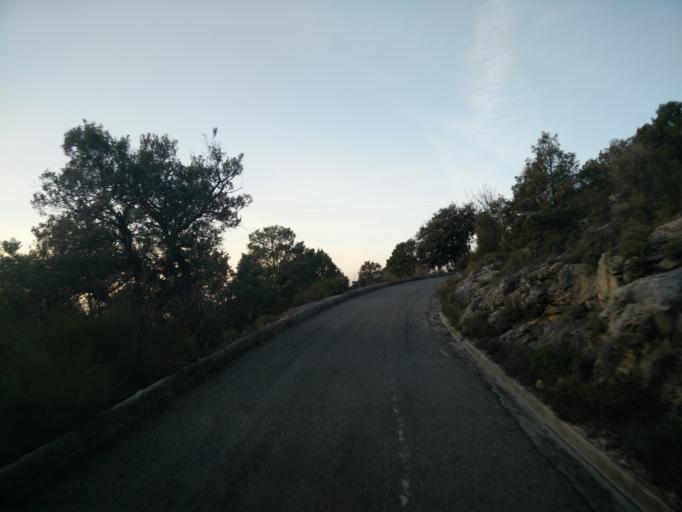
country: FR
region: Provence-Alpes-Cote d'Azur
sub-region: Departement des Alpes-Maritimes
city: Peille
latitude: 43.7907
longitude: 7.4026
